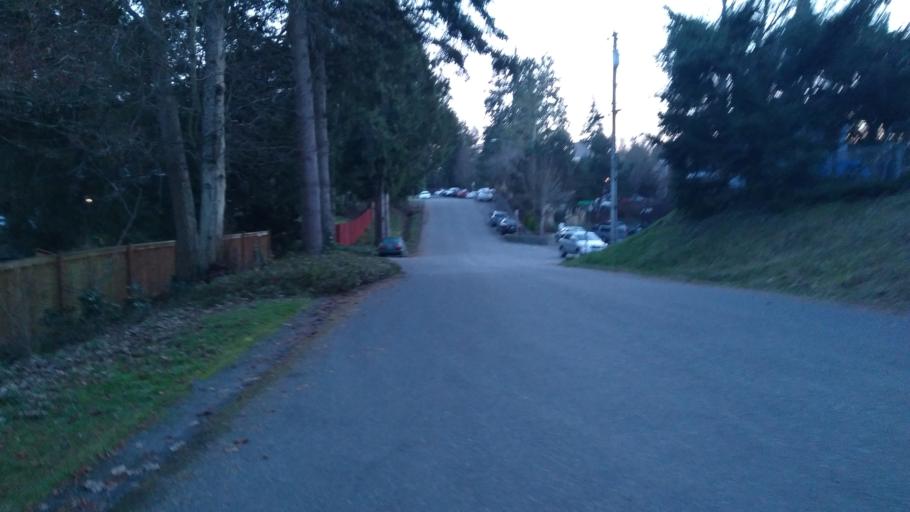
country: US
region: Washington
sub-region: Snohomish County
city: Esperance
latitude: 47.7916
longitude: -122.3539
